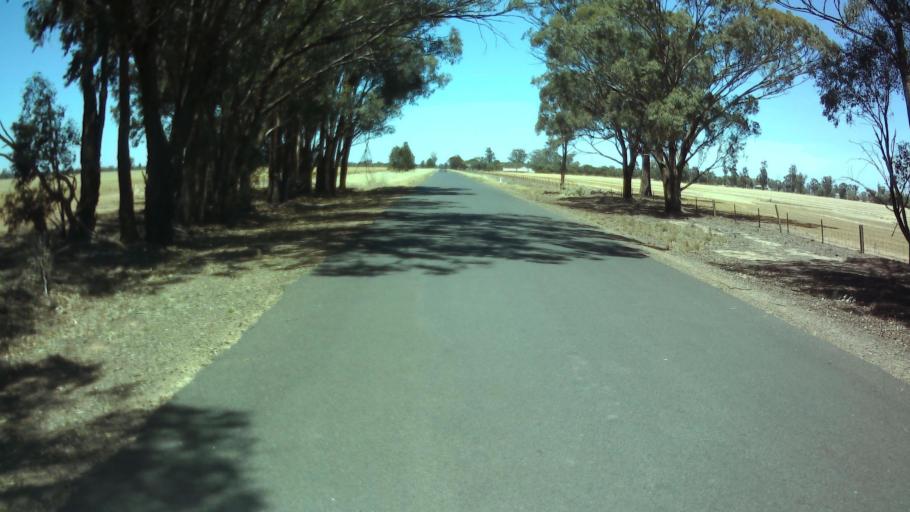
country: AU
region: New South Wales
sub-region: Weddin
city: Grenfell
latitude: -34.0253
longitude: 147.7918
